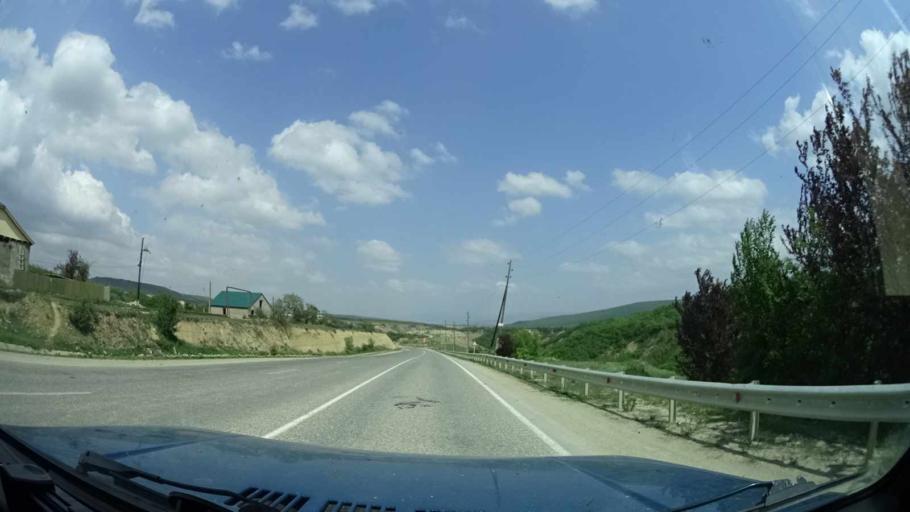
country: RU
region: Dagestan
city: Erpeli
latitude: 42.8125
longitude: 47.0232
